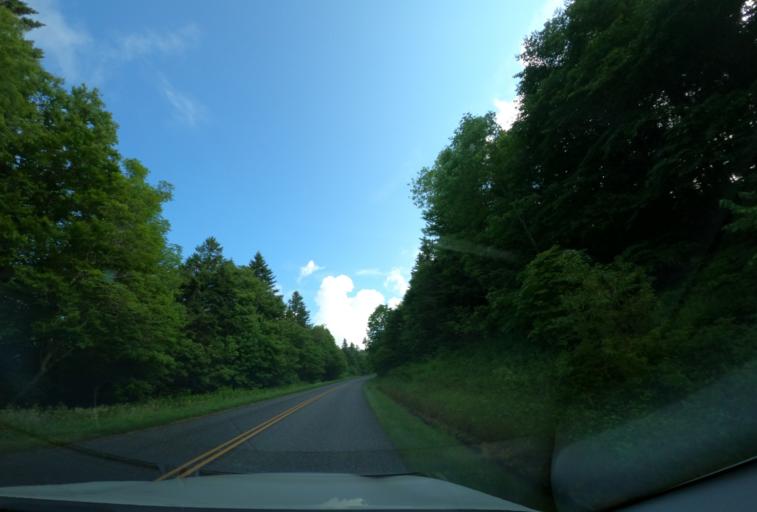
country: US
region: North Carolina
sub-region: Haywood County
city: Hazelwood
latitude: 35.3220
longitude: -82.9649
